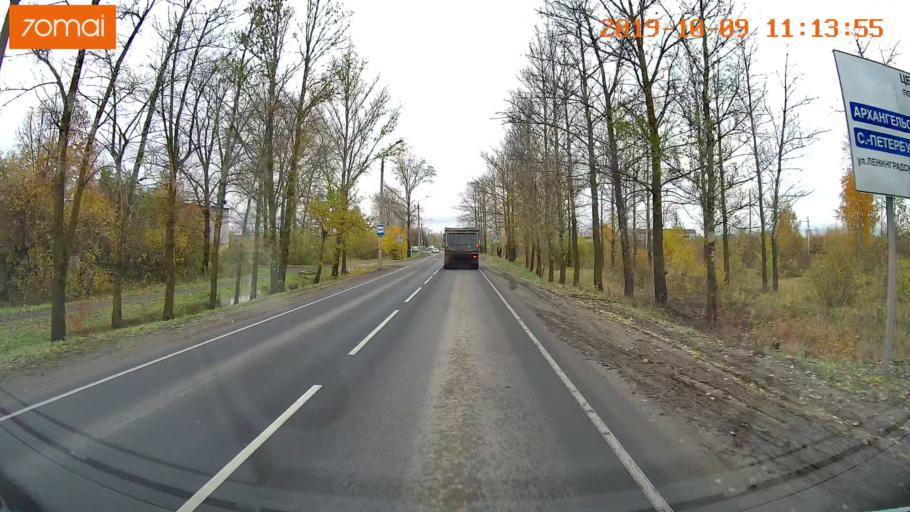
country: RU
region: Vologda
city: Vologda
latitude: 59.1851
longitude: 39.8483
